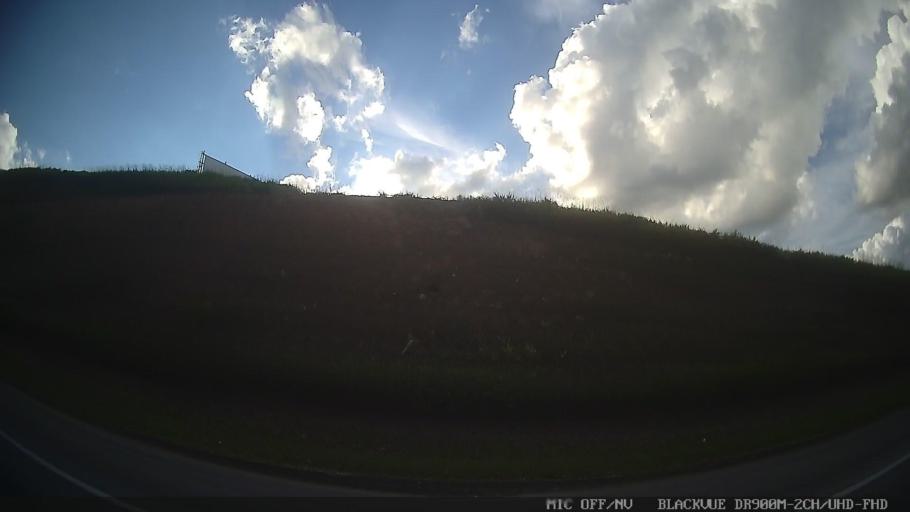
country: BR
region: Sao Paulo
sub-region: Braganca Paulista
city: Braganca Paulista
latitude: -22.9527
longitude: -46.4799
